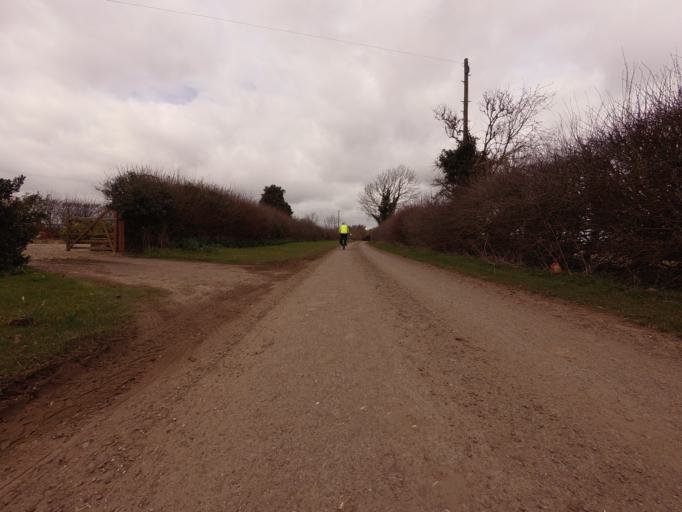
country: GB
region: England
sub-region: Lincolnshire
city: Grantham
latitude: 52.8710
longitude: -0.6591
